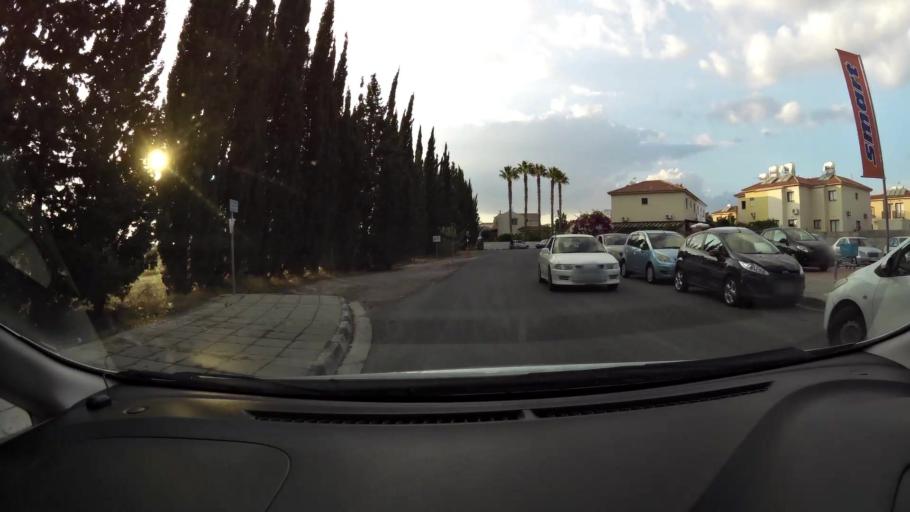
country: CY
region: Larnaka
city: Meneou
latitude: 34.8614
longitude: 33.5870
